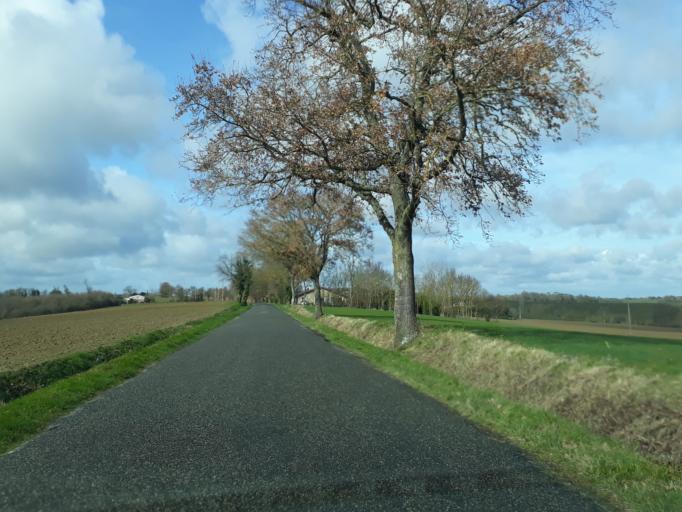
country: FR
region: Midi-Pyrenees
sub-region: Departement du Gers
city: Pujaudran
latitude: 43.6295
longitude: 1.0174
